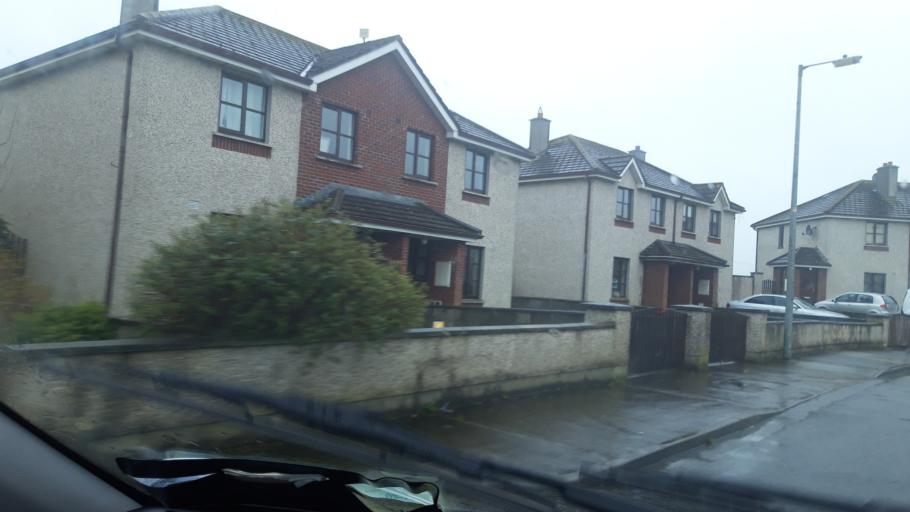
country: IE
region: Leinster
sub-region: Kilkenny
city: Kilkenny
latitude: 52.6589
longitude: -7.2285
